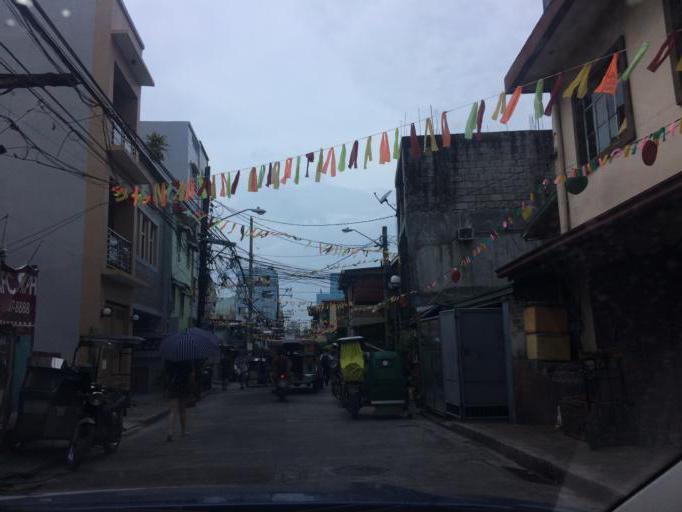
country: PH
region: Metro Manila
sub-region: Makati City
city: Makati City
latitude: 14.5472
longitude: 121.0023
